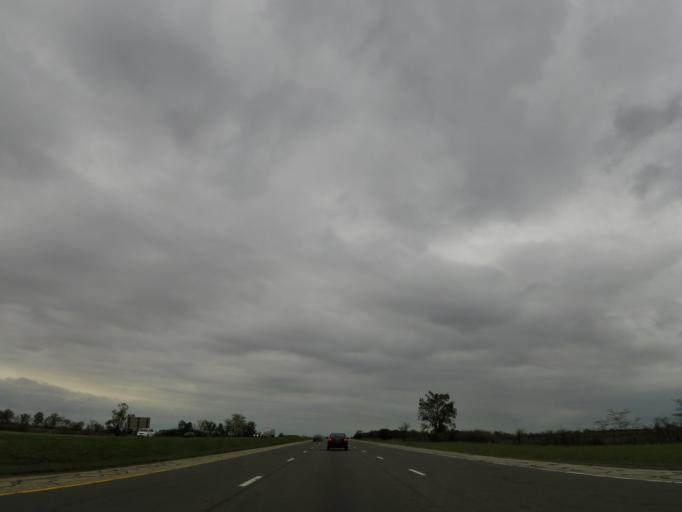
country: US
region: Ohio
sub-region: Madison County
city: Bethel
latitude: 39.6977
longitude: -83.4528
